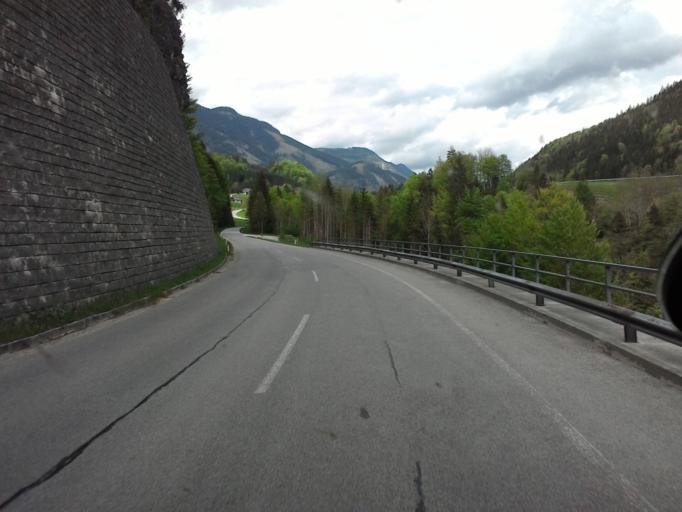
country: AT
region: Styria
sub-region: Politischer Bezirk Liezen
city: Palfau
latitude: 47.6907
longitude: 14.7772
